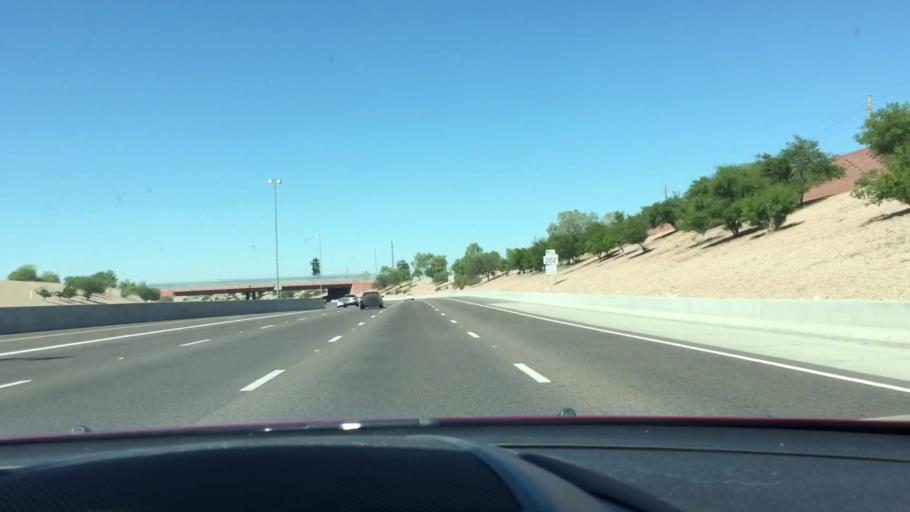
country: US
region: Arizona
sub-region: Maricopa County
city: Mesa
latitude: 33.4672
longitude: -111.8188
